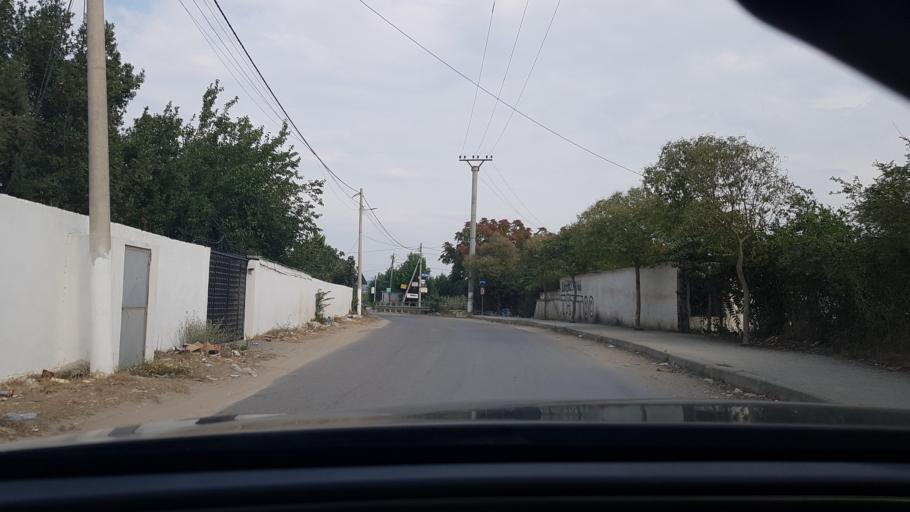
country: AL
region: Durres
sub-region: Rrethi i Durresit
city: Katundi i Ri
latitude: 41.4866
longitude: 19.5185
